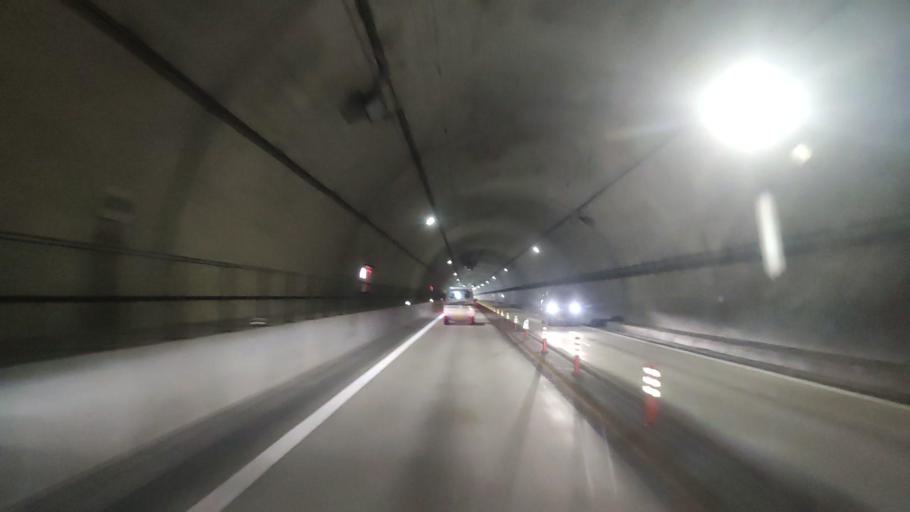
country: JP
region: Wakayama
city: Tanabe
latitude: 33.6289
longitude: 135.4151
